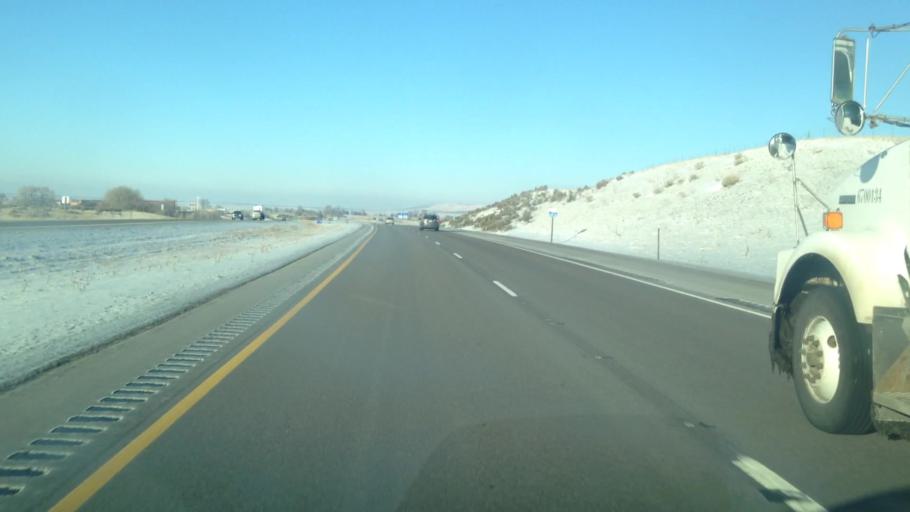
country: US
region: Idaho
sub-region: Bingham County
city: Fort Hall
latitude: 43.0074
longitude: -112.4086
